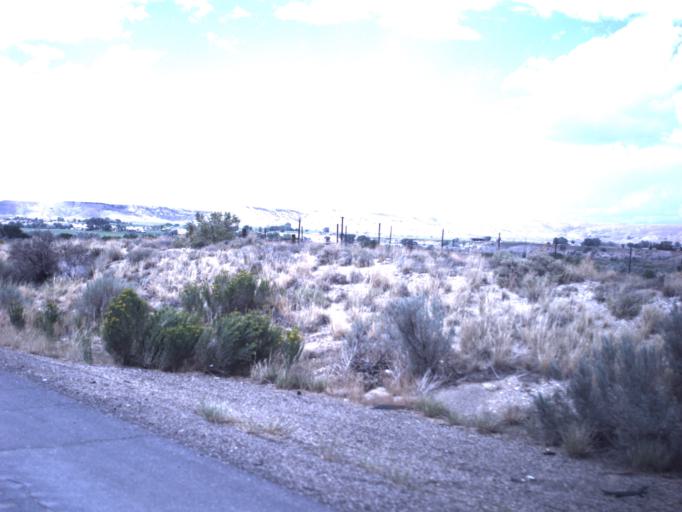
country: US
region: Utah
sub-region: Duchesne County
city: Duchesne
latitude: 40.1688
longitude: -110.2994
